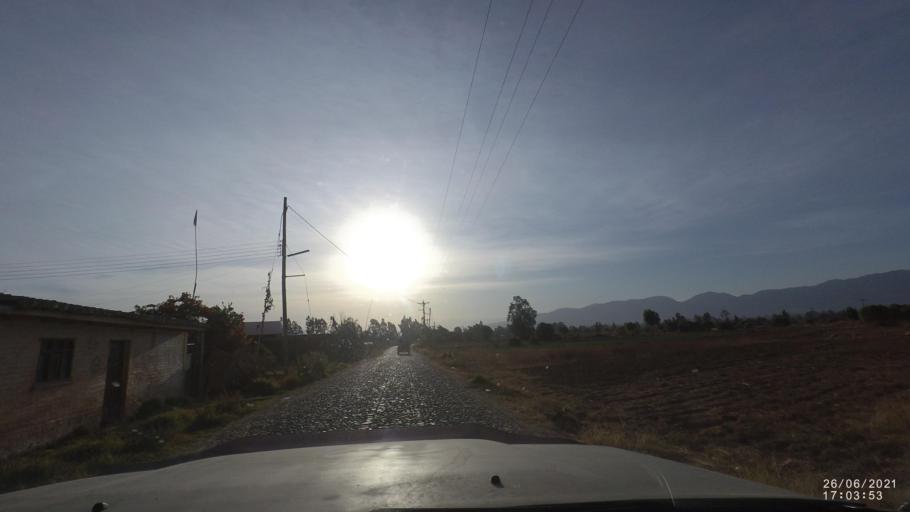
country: BO
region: Cochabamba
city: Cliza
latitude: -17.6390
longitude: -65.9124
